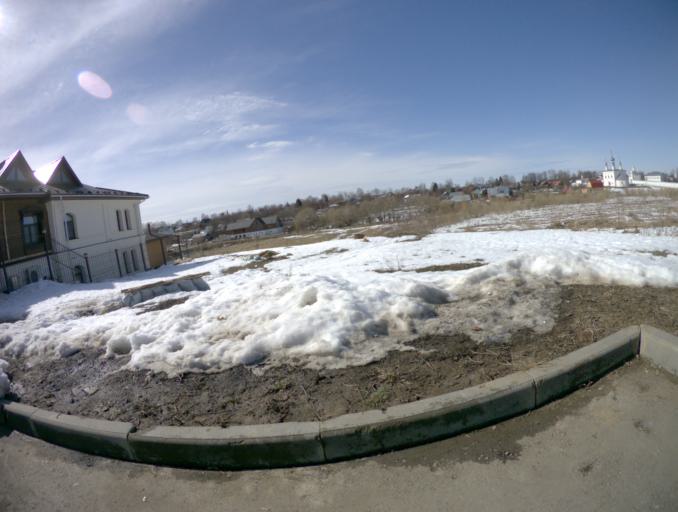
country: RU
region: Vladimir
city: Suzdal'
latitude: 56.4256
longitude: 40.4395
